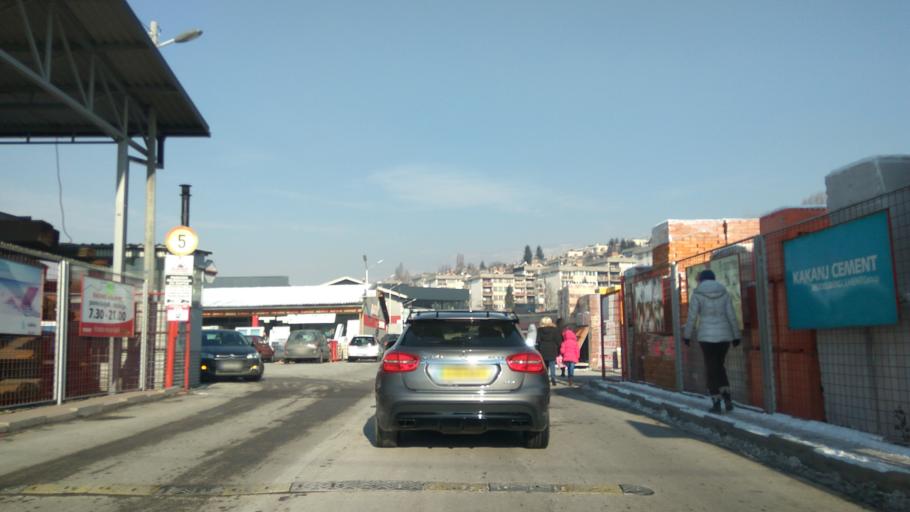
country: BA
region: Federation of Bosnia and Herzegovina
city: Kobilja Glava
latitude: 43.8646
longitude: 18.4023
